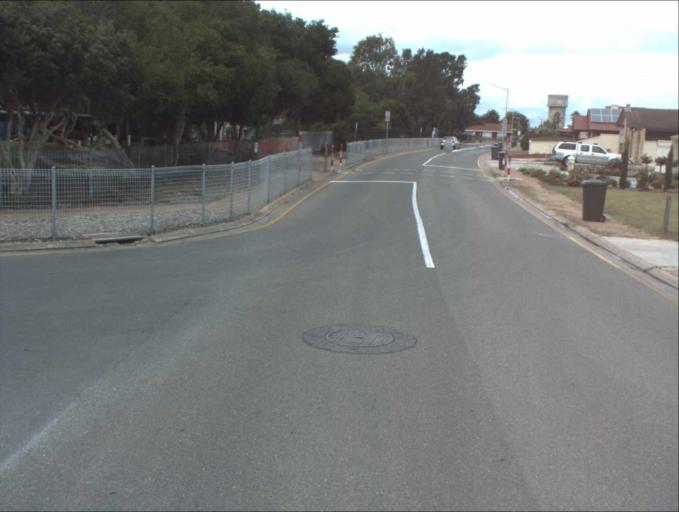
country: AU
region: South Australia
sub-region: Port Adelaide Enfield
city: Birkenhead
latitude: -34.7897
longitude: 138.4966
